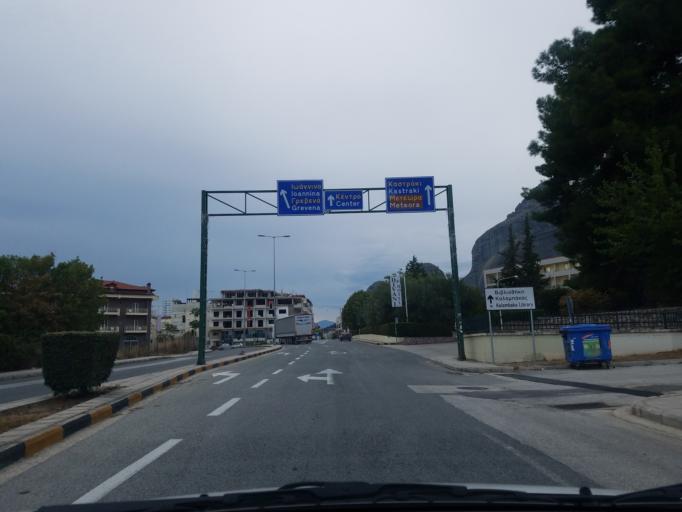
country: GR
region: Thessaly
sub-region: Trikala
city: Kalampaka
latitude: 39.7017
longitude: 21.6339
